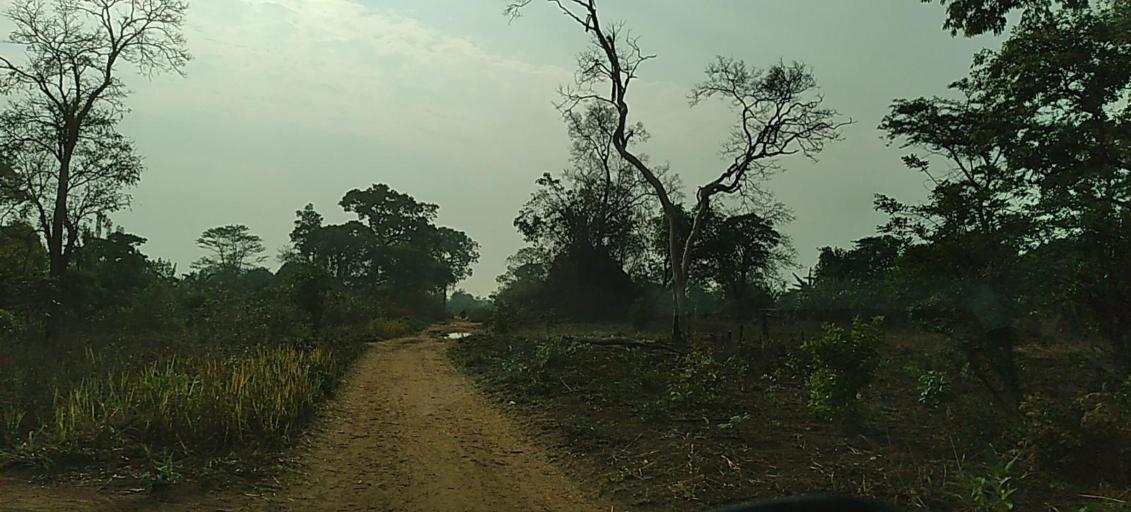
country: ZM
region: North-Western
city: Solwezi
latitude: -12.3539
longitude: 26.5405
